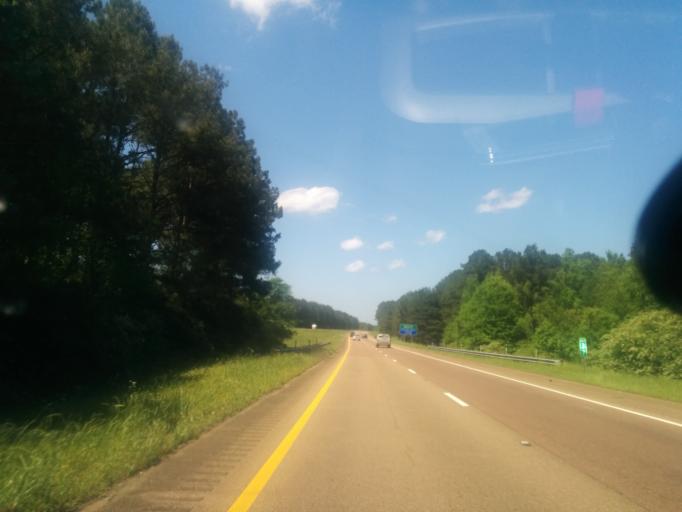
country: US
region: Mississippi
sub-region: Lincoln County
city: Brookhaven
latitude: 31.5291
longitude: -90.4792
